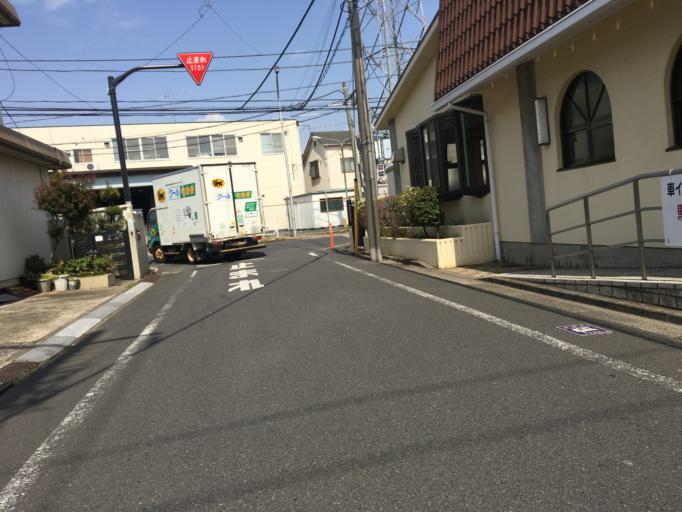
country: JP
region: Tokyo
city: Kamirenjaku
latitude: 35.6903
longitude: 139.5445
